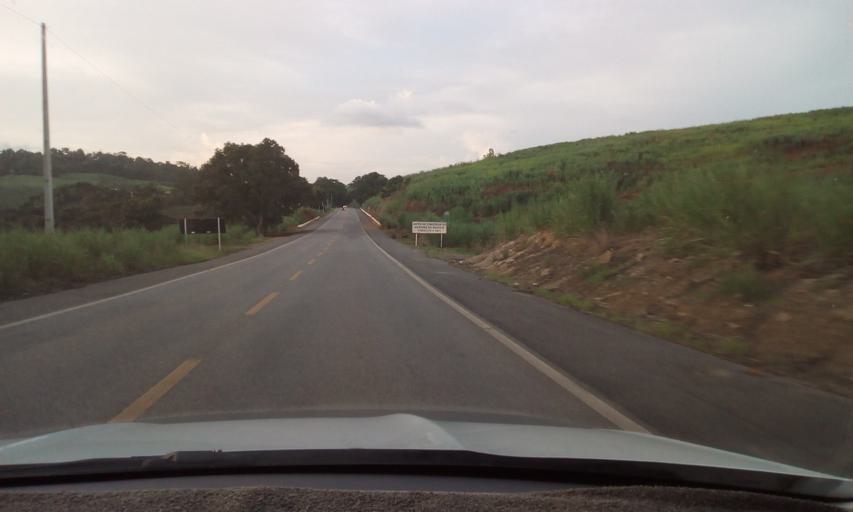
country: BR
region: Pernambuco
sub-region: Vicencia
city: Vicencia
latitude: -7.6472
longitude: -35.2529
